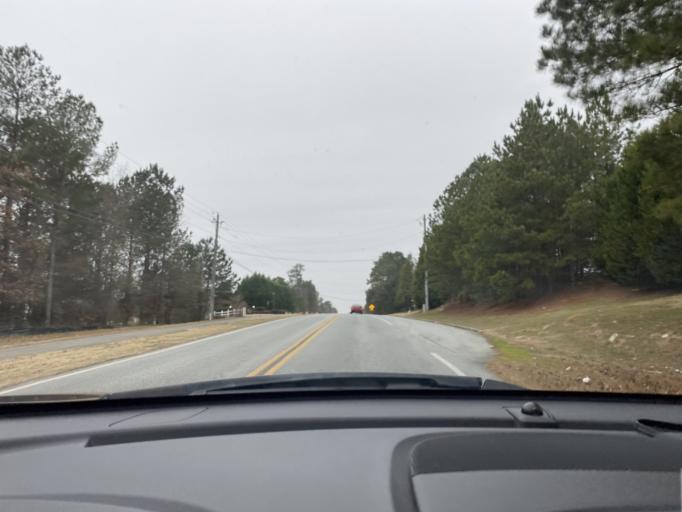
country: US
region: Georgia
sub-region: Gwinnett County
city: Dacula
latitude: 33.9147
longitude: -83.8790
